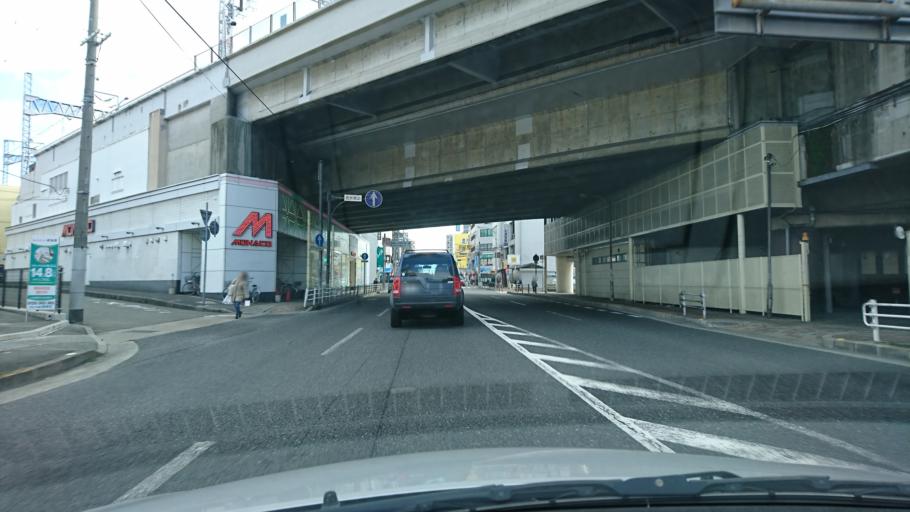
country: JP
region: Hyogo
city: Akashi
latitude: 34.6670
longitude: 134.9620
